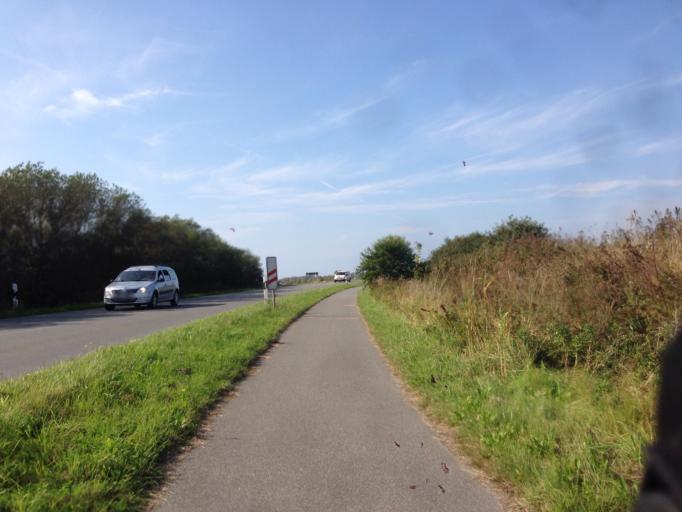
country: DE
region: Schleswig-Holstein
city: Keitum
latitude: 54.8910
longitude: 8.3617
